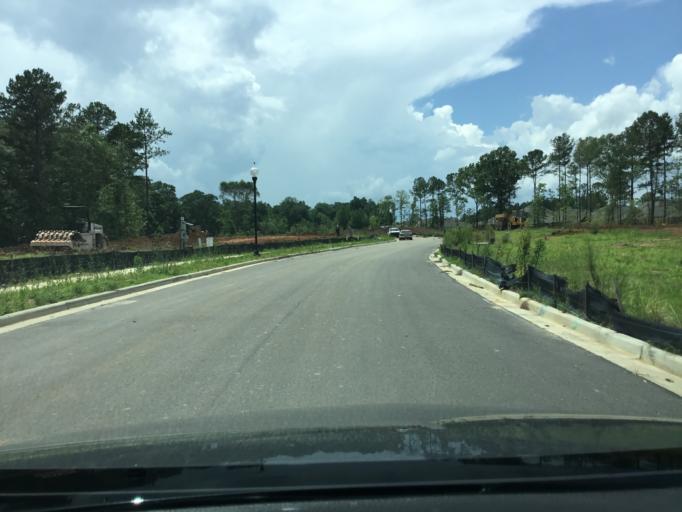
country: US
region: Alabama
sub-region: Montgomery County
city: Pike Road
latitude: 32.3339
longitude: -86.0728
